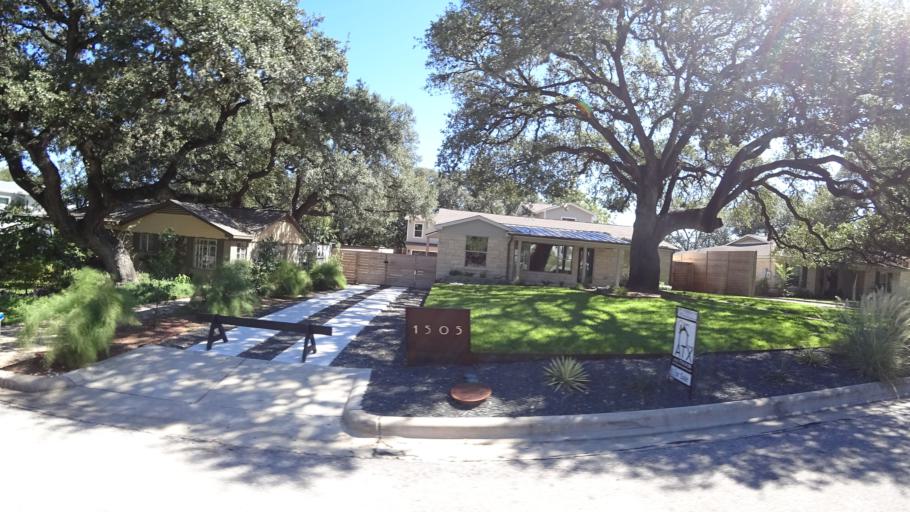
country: US
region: Texas
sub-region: Travis County
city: Austin
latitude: 30.2442
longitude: -97.7382
